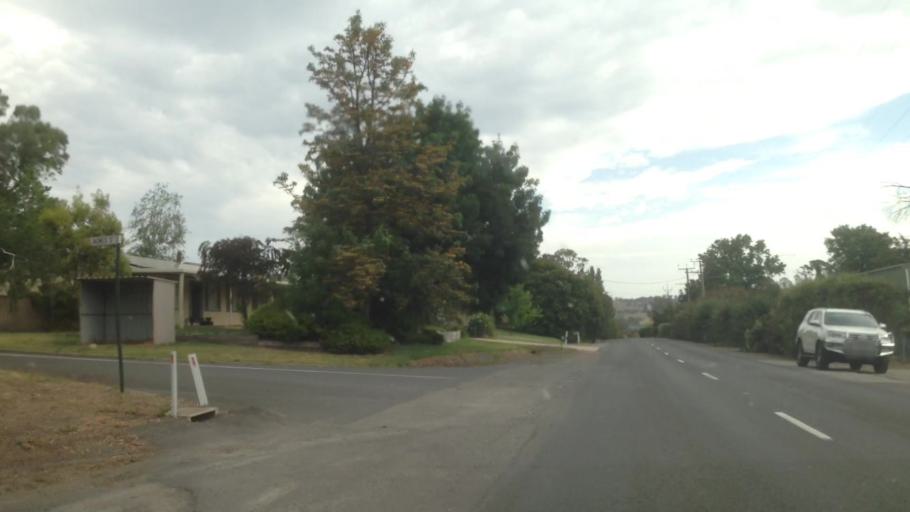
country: AU
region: South Australia
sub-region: Adelaide Hills
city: Gumeracha
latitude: -34.7978
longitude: 138.8993
